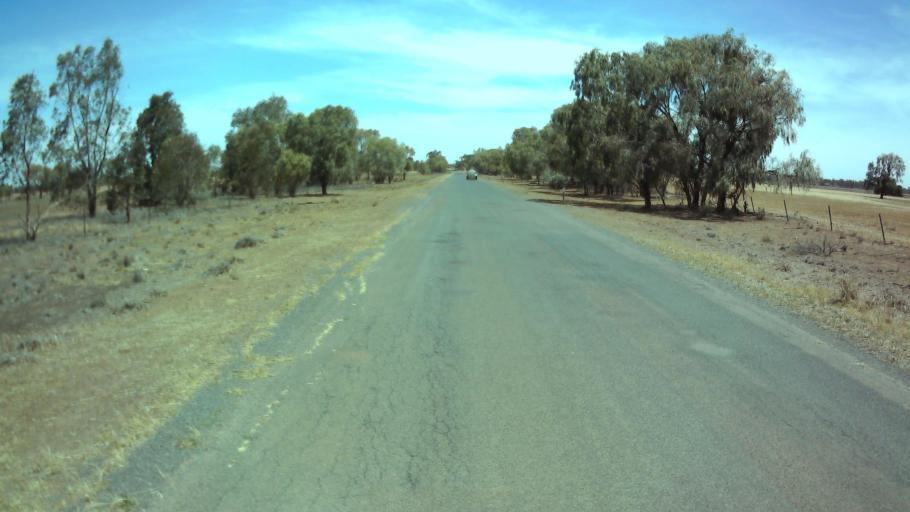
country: AU
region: New South Wales
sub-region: Weddin
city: Grenfell
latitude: -33.8257
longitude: 147.7467
